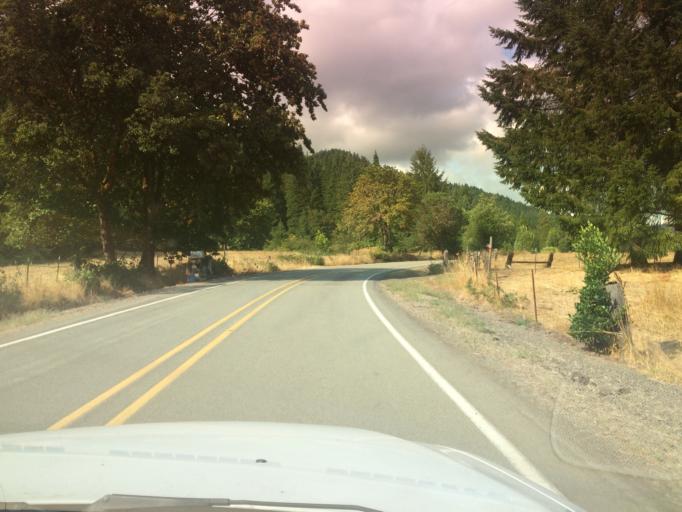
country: US
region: Oregon
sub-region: Douglas County
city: Sutherlin
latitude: 43.3653
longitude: -123.5767
